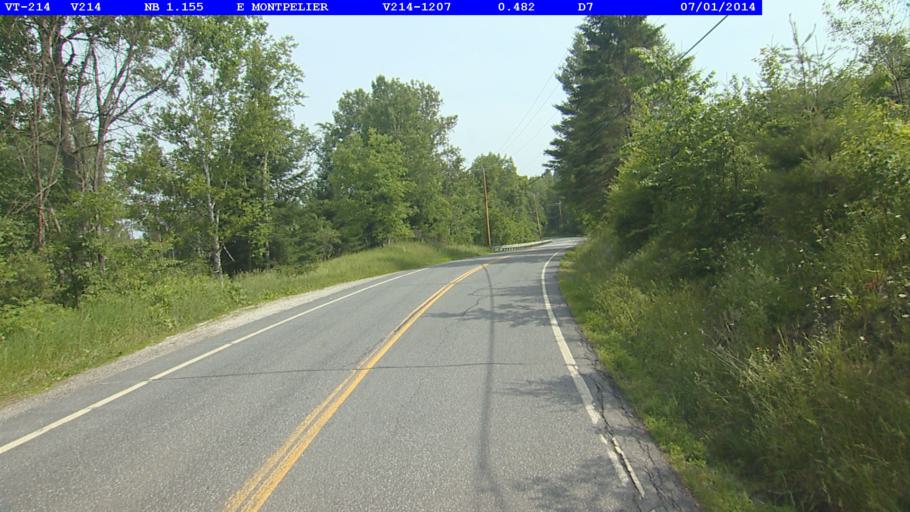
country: US
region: Vermont
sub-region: Washington County
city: Barre
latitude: 44.2922
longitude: -72.4445
